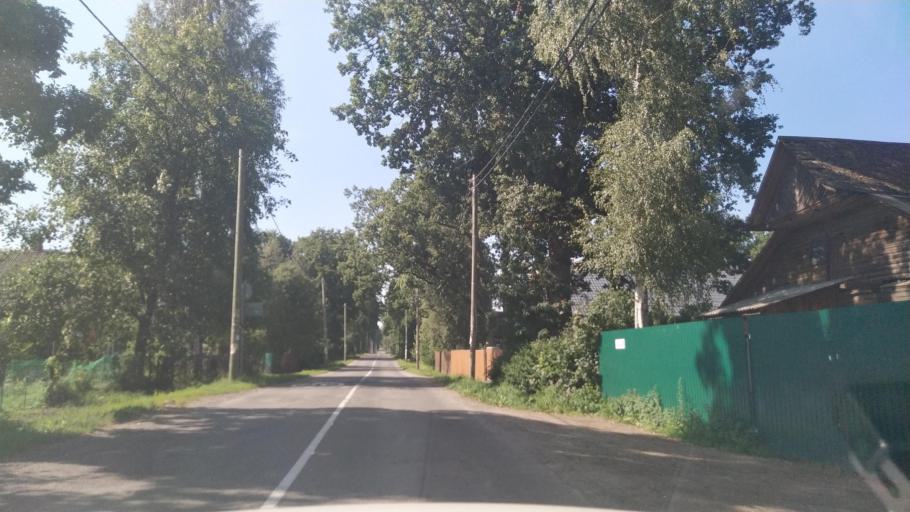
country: RU
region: Leningrad
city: Siverskiy
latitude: 59.2956
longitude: 30.0727
